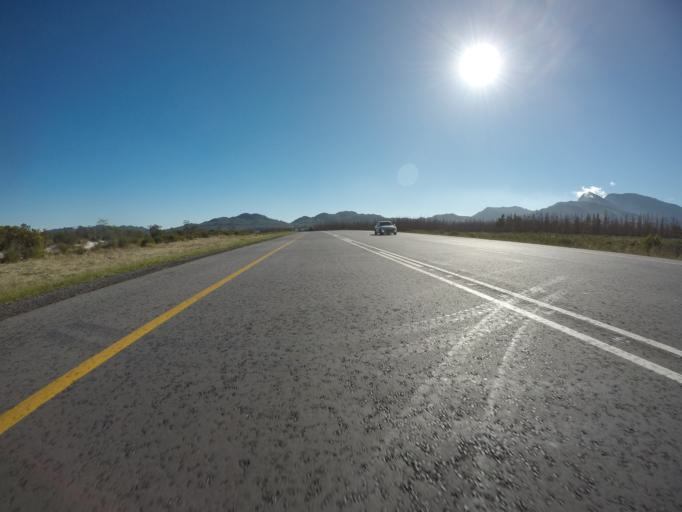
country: ZA
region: Western Cape
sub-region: Overberg District Municipality
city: Grabouw
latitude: -34.1540
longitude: 18.9680
